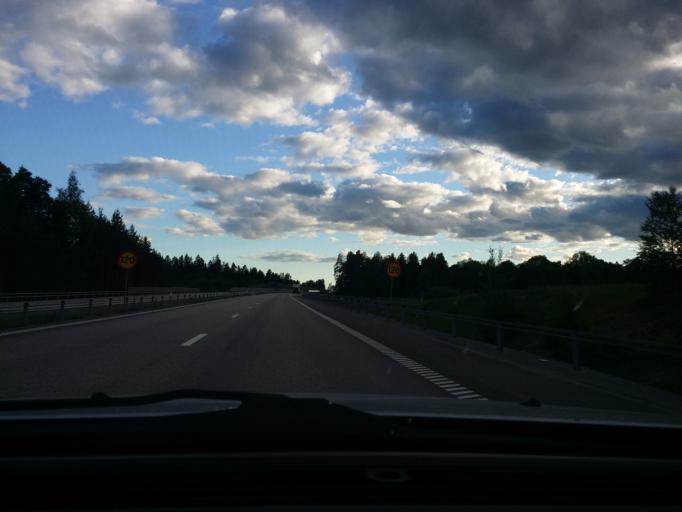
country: SE
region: Uppsala
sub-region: Enkopings Kommun
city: Enkoping
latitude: 59.6468
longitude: 17.0571
